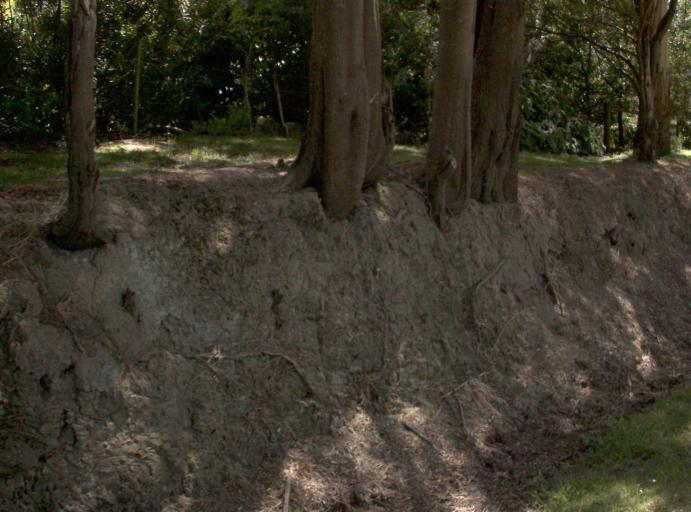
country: AU
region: Victoria
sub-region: Baw Baw
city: Warragul
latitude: -38.2950
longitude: 145.9014
